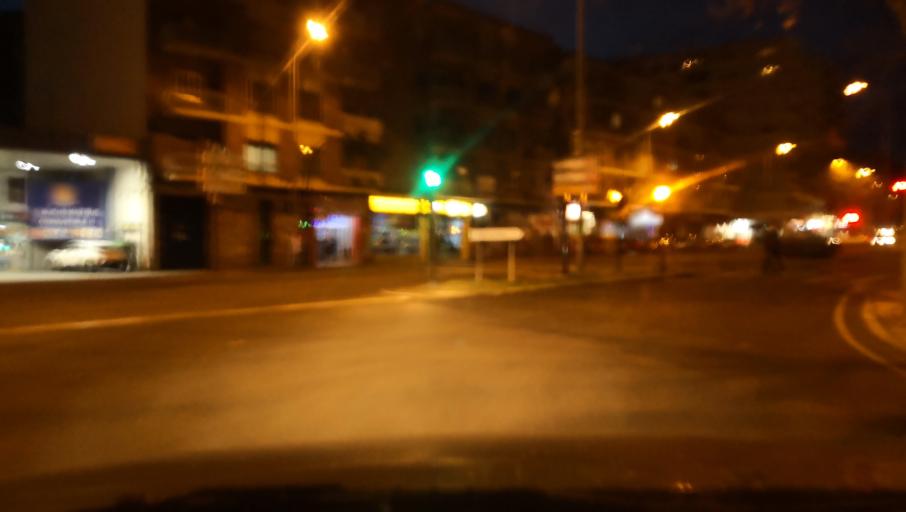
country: ES
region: Castille and Leon
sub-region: Provincia de Zamora
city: Zamora
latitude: 41.5109
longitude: -5.7360
